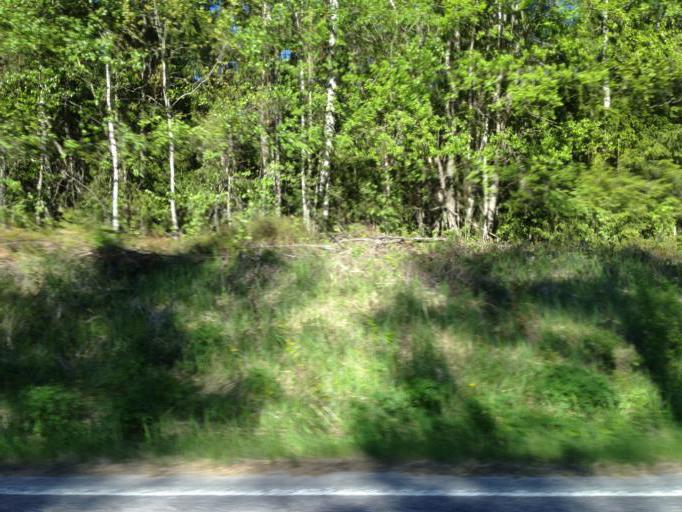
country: FI
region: Uusimaa
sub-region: Helsinki
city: Espoo
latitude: 60.2710
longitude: 24.5942
